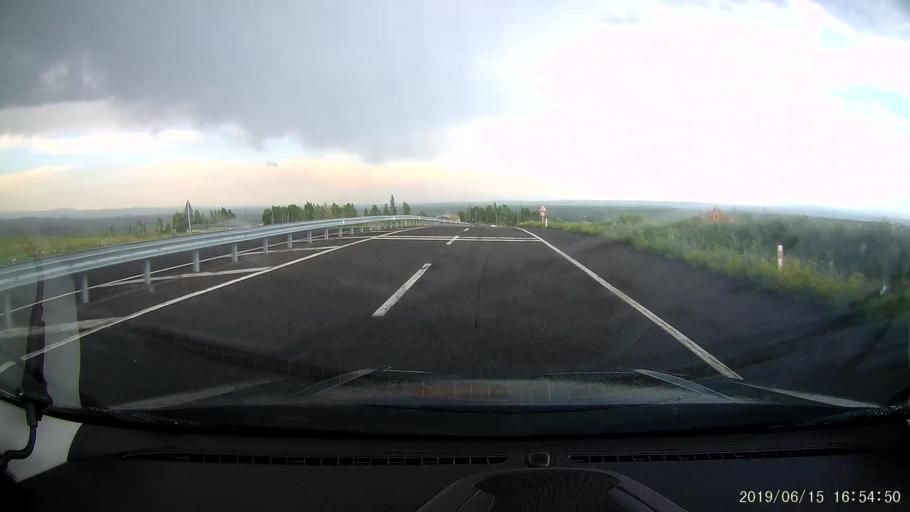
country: TR
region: Kars
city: Susuz
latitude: 40.7883
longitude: 43.1335
